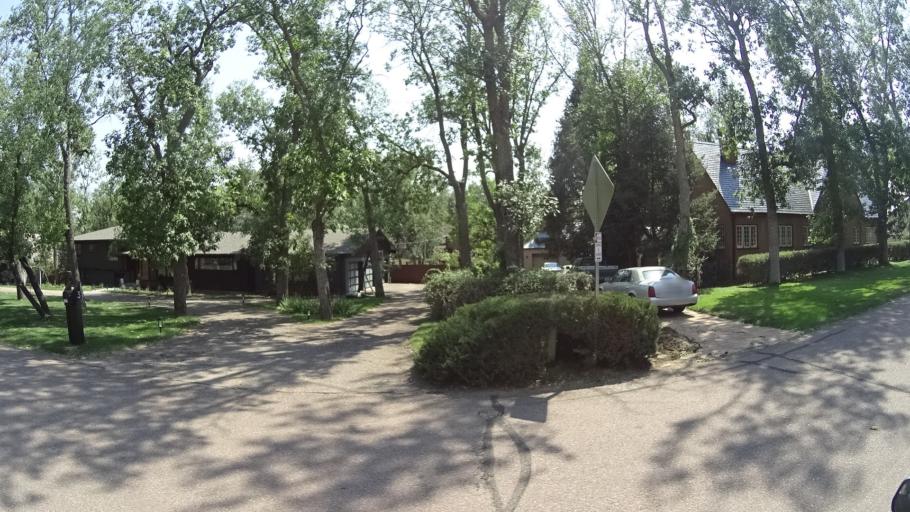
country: US
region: Colorado
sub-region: El Paso County
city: Colorado Springs
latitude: 38.7896
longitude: -104.8457
